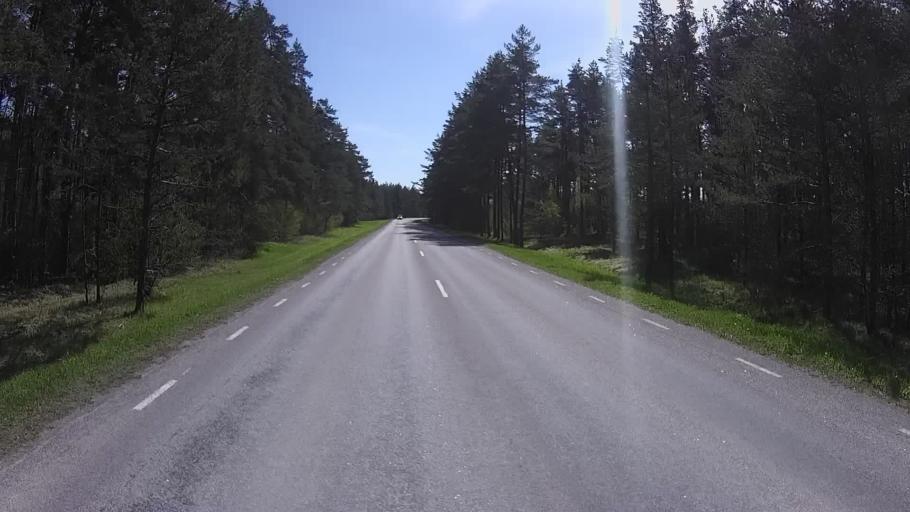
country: EE
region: Laeaene
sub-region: Haapsalu linn
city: Haapsalu
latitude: 58.9123
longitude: 23.5570
